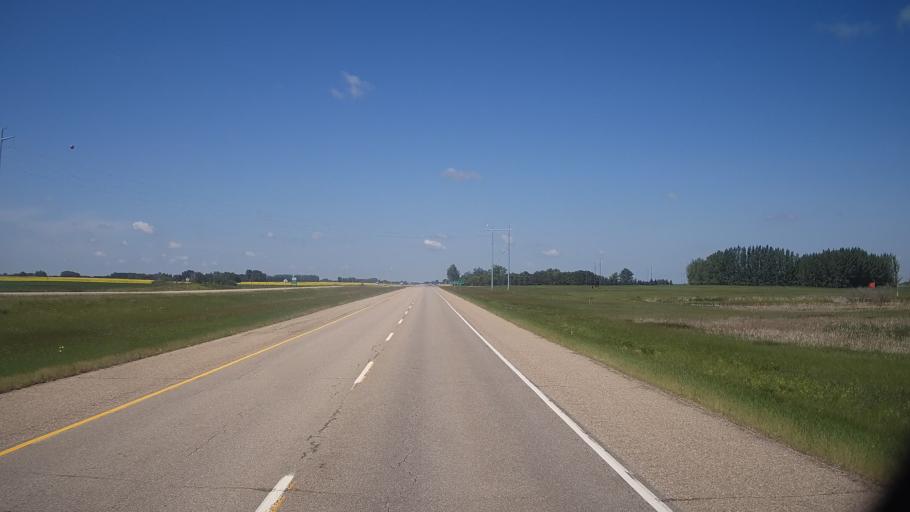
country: CA
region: Saskatchewan
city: Saskatoon
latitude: 51.9981
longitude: -106.3056
